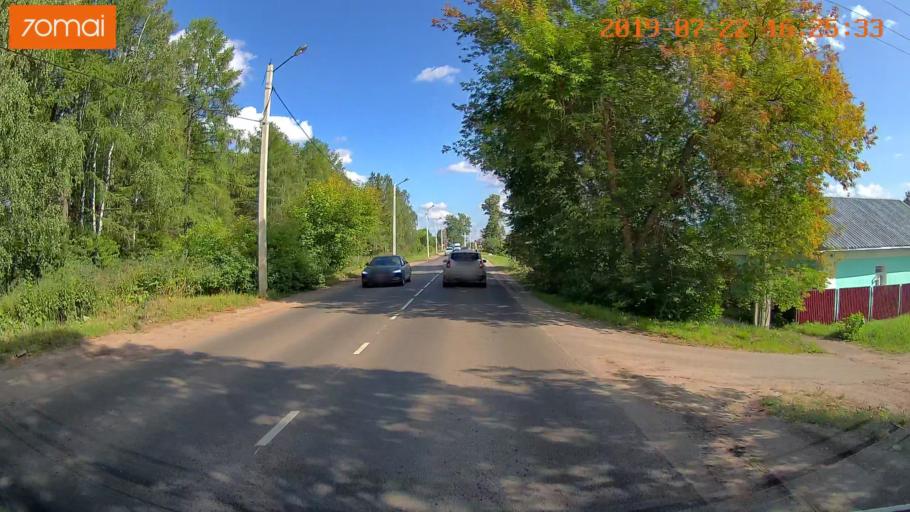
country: RU
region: Ivanovo
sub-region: Gorod Ivanovo
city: Ivanovo
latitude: 57.0529
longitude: 40.9259
